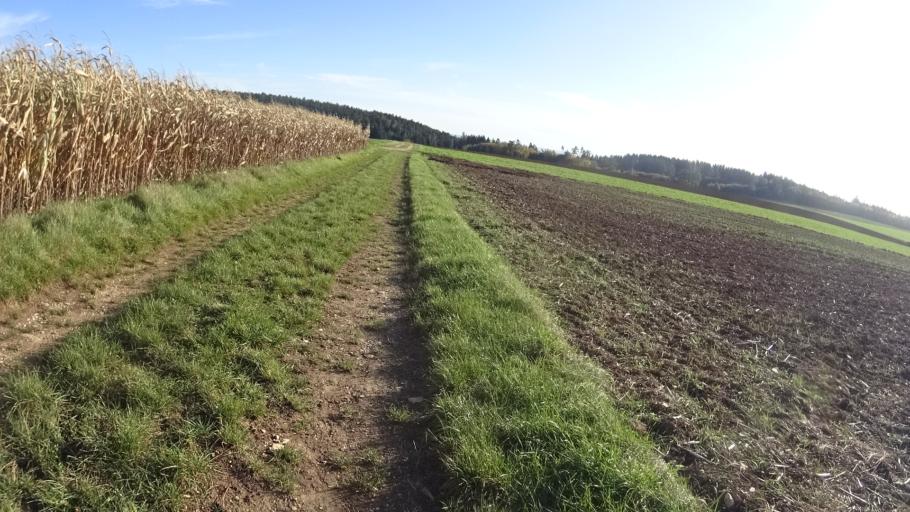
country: DE
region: Bavaria
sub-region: Upper Bavaria
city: Bohmfeld
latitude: 48.8547
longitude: 11.3617
